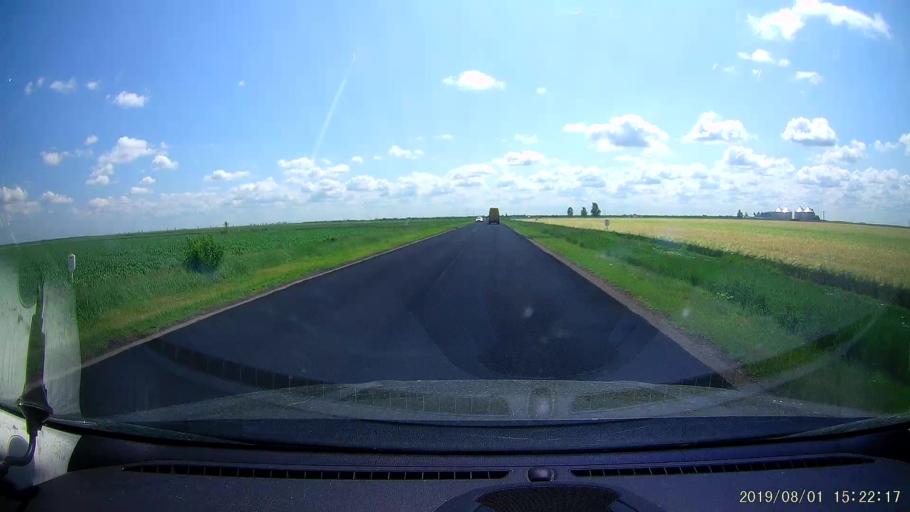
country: RO
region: Braila
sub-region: Comuna Viziru
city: Lanurile
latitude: 45.0559
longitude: 27.7791
